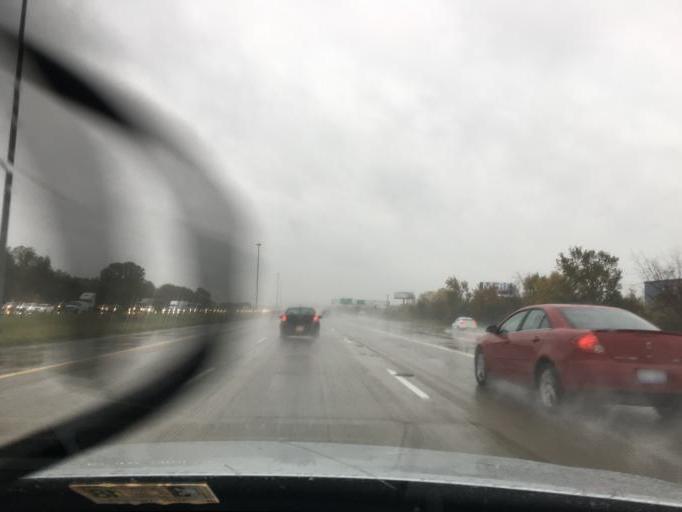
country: US
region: Michigan
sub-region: Wayne County
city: Allen Park
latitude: 42.2657
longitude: -83.2403
